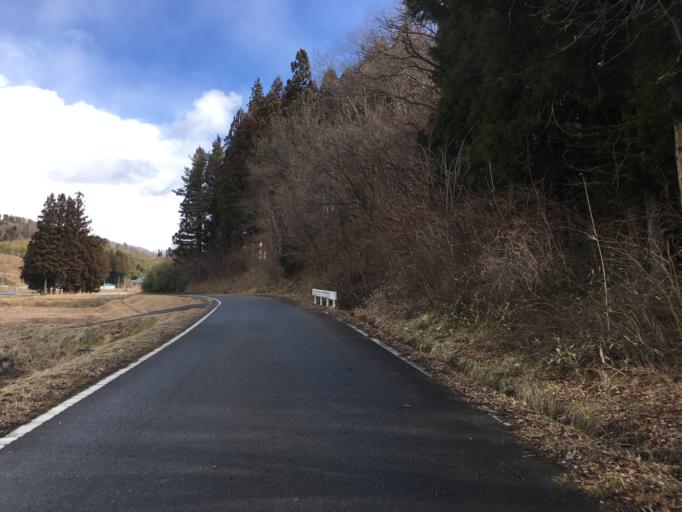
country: JP
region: Fukushima
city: Ishikawa
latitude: 37.2135
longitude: 140.5586
